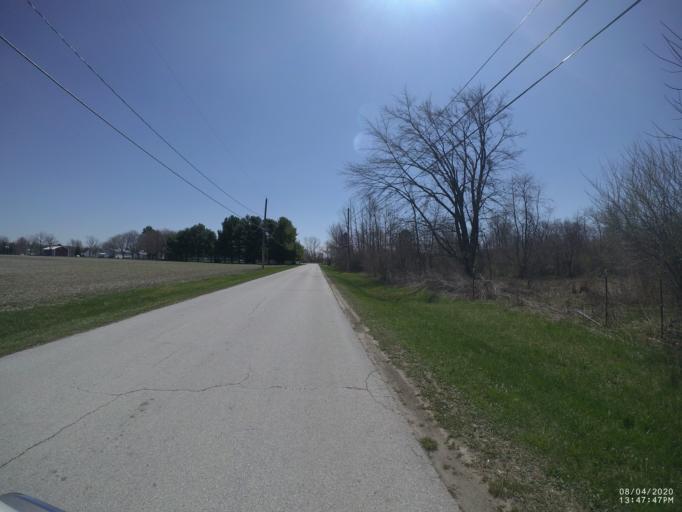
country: US
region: Ohio
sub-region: Sandusky County
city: Gibsonburg
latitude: 41.3135
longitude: -83.2839
